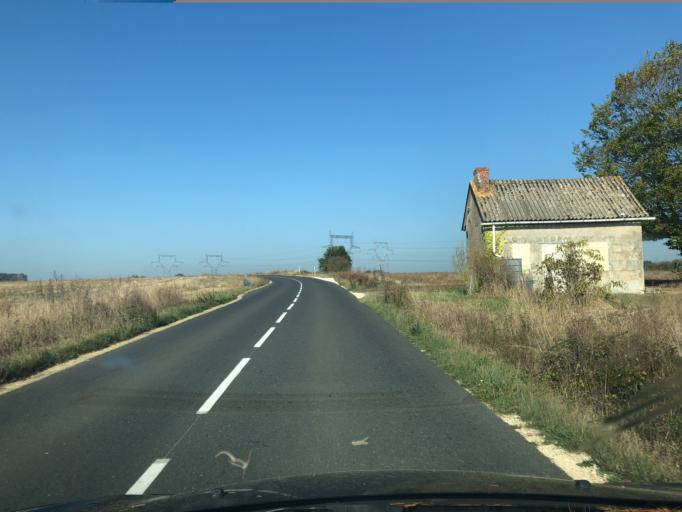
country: FR
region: Centre
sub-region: Departement d'Indre-et-Loire
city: Cerelles
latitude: 47.4907
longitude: 0.6591
